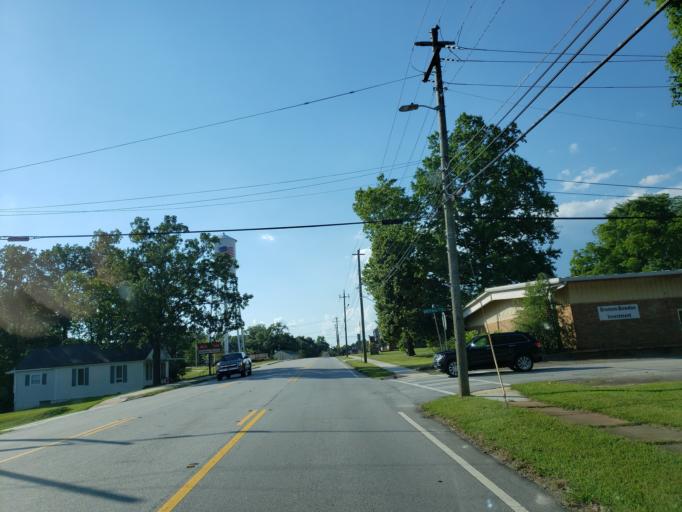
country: US
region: Georgia
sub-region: Haralson County
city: Bremen
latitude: 33.7235
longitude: -85.1474
